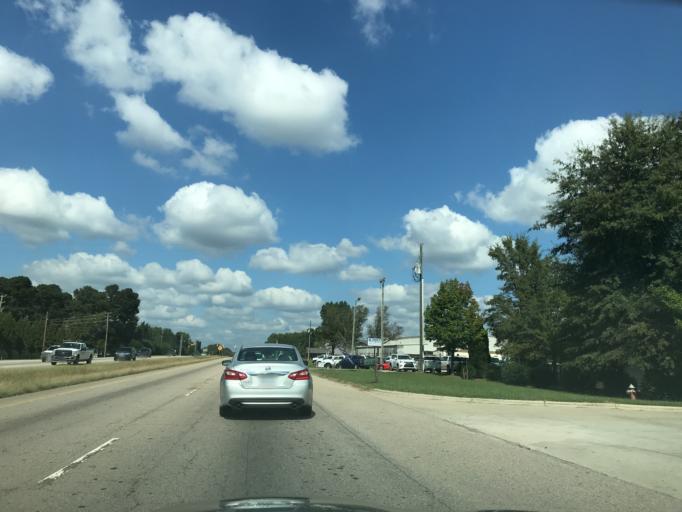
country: US
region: North Carolina
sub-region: Wake County
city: Wake Forest
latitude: 35.8956
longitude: -78.5586
